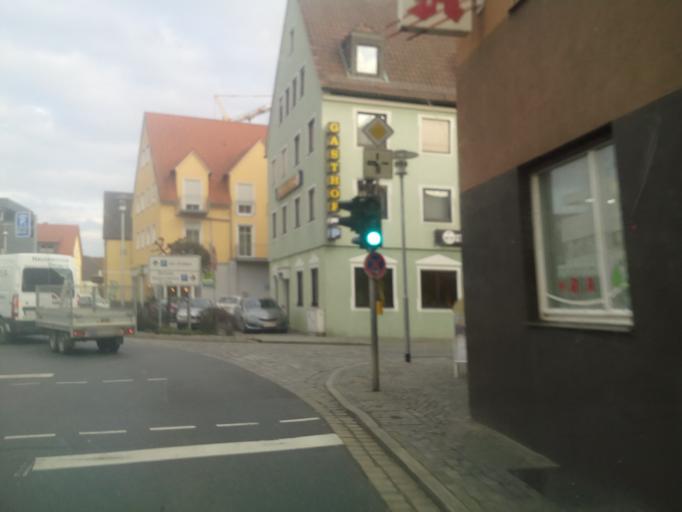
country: DE
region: Bavaria
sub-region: Regierungsbezirk Mittelfranken
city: Hochstadt an der Aisch
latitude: 49.7055
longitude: 10.8054
